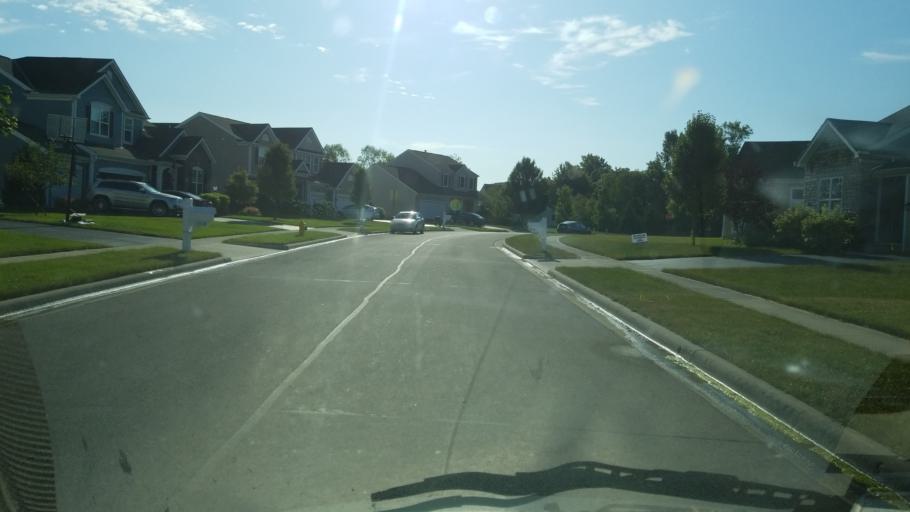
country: US
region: Ohio
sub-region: Delaware County
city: Lewis Center
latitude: 40.1834
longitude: -83.0035
